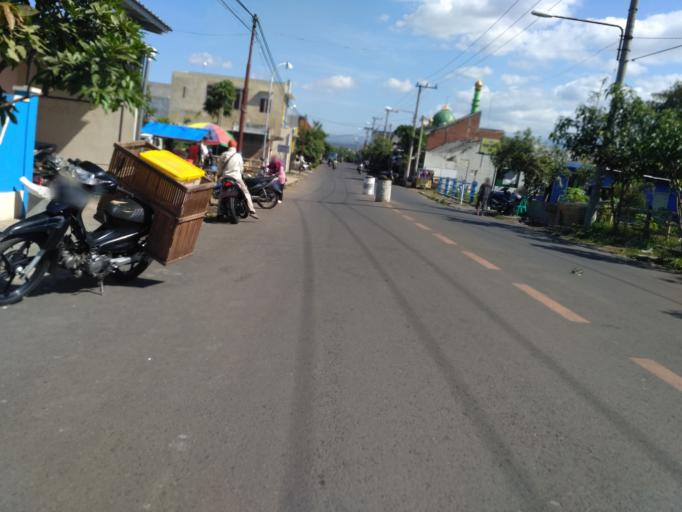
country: ID
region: East Java
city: Singosari
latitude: -7.9116
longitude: 112.6666
